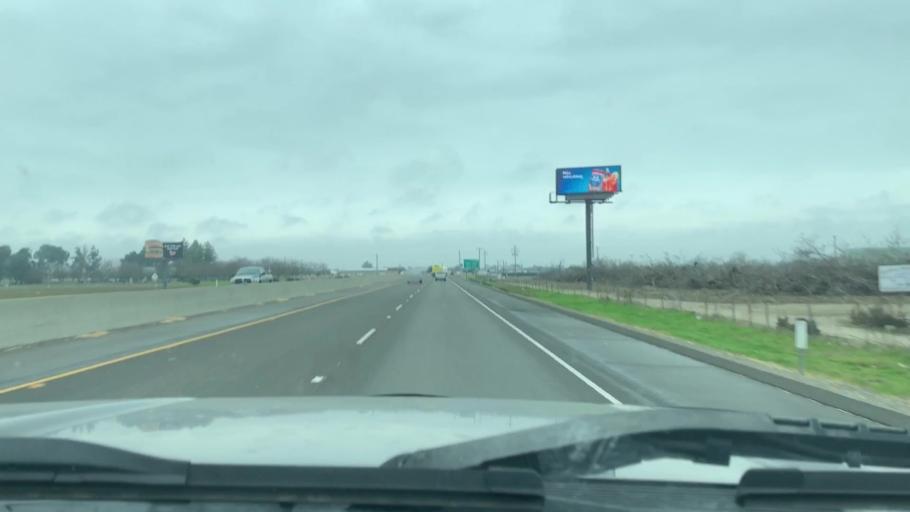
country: US
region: California
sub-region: Kings County
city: Armona
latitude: 36.3158
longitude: -119.6871
